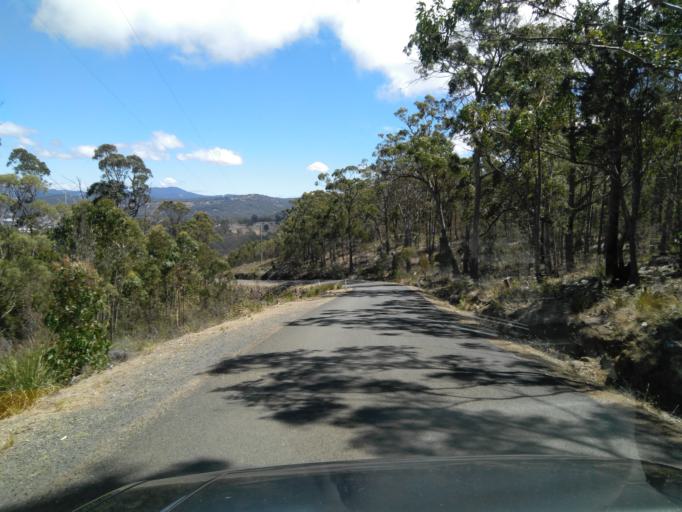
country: AU
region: Tasmania
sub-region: Kingborough
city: Taroona
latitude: -42.9499
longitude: 147.3244
